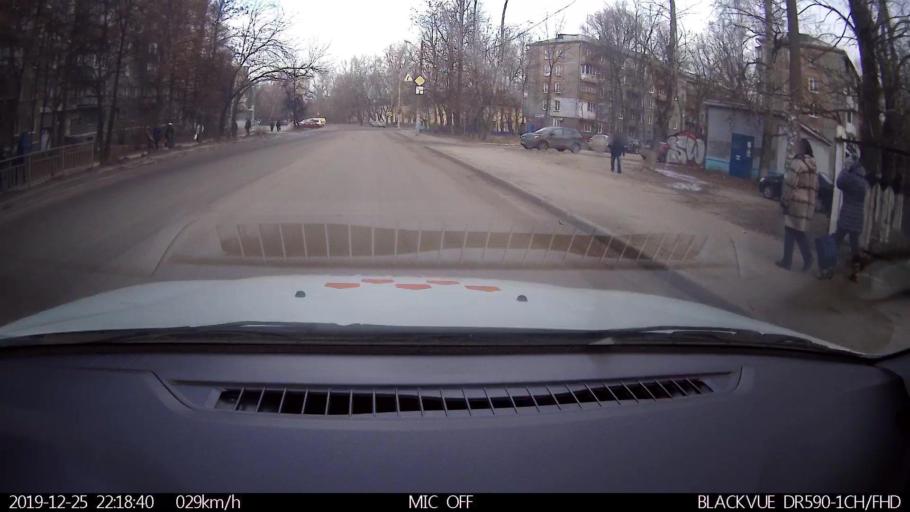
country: RU
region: Nizjnij Novgorod
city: Gorbatovka
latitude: 56.3363
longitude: 43.8399
